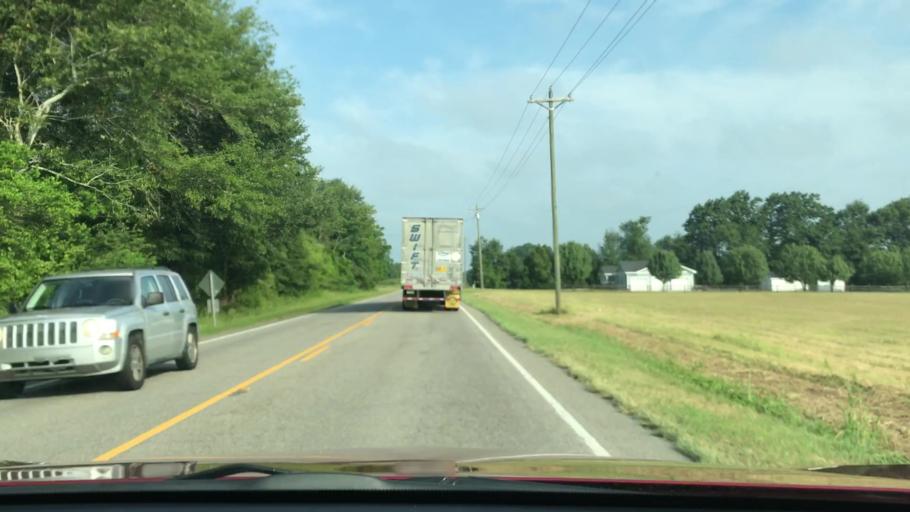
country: US
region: South Carolina
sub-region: Barnwell County
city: Blackville
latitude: 33.6071
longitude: -81.2688
